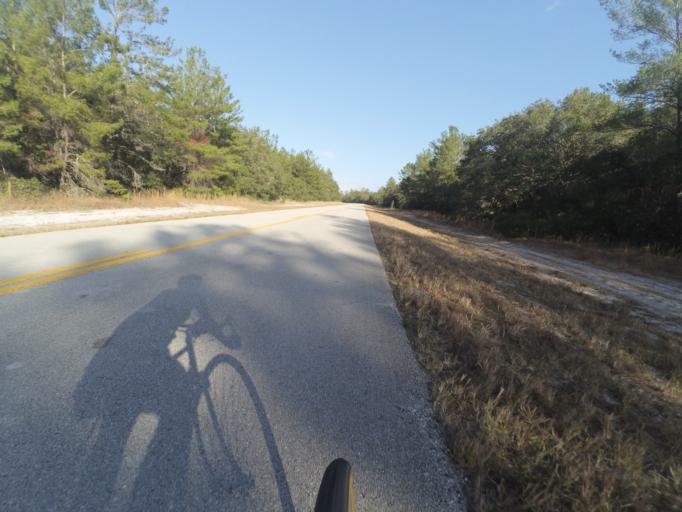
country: US
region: Florida
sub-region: Lake County
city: Astor
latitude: 29.0988
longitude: -81.5649
